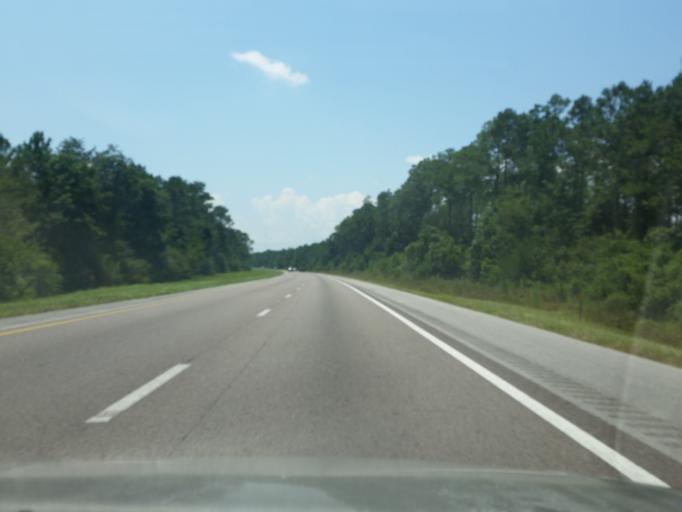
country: US
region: Florida
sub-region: Escambia County
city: Cantonment
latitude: 30.5812
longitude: -87.4837
